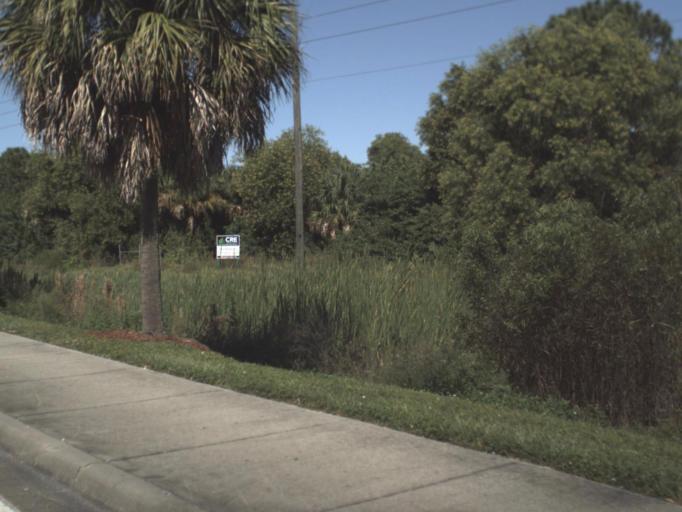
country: US
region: Florida
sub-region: Collier County
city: Vineyards
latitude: 26.2117
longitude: -81.7406
